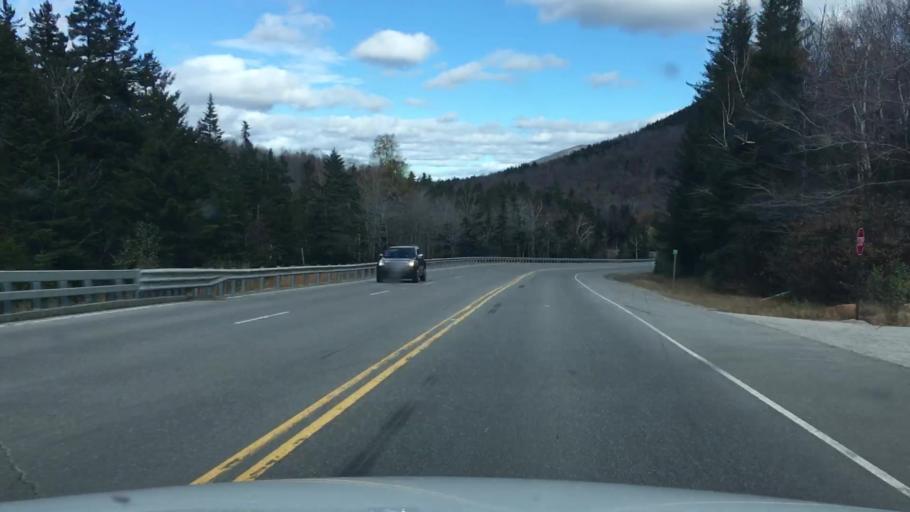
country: US
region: New Hampshire
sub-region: Coos County
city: Gorham
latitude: 44.2716
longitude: -71.2348
